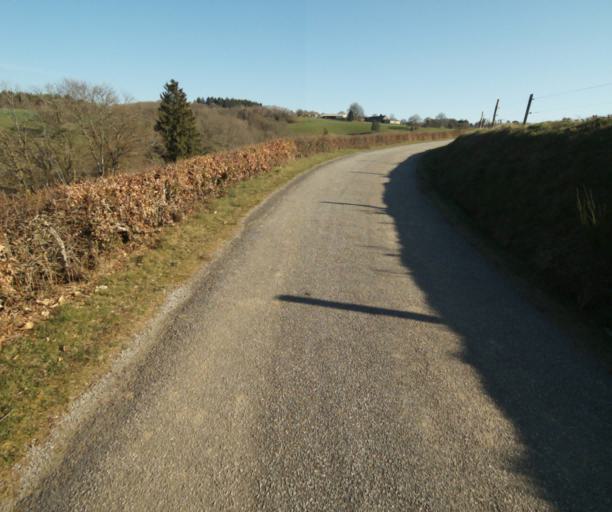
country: FR
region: Limousin
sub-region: Departement de la Correze
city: Chamboulive
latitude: 45.4870
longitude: 1.7322
